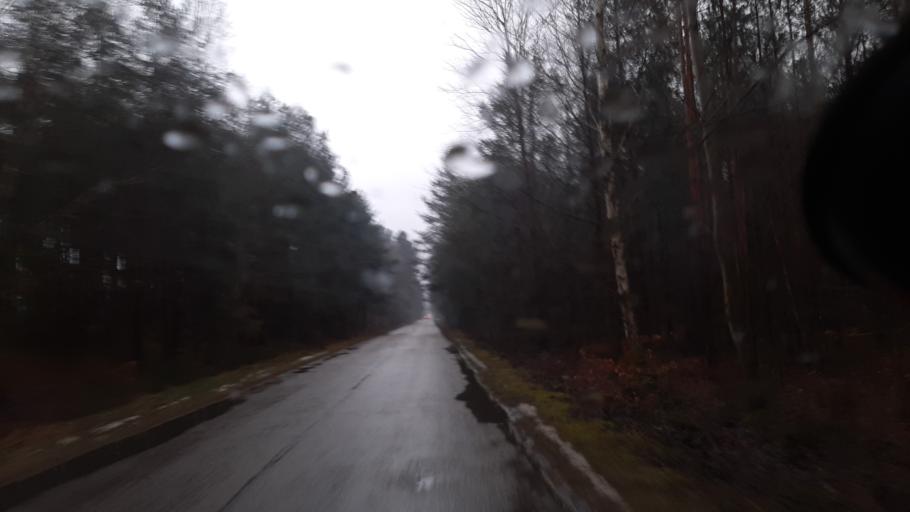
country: PL
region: Lublin Voivodeship
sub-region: Powiat lubartowski
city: Kamionka
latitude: 51.5091
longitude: 22.4902
